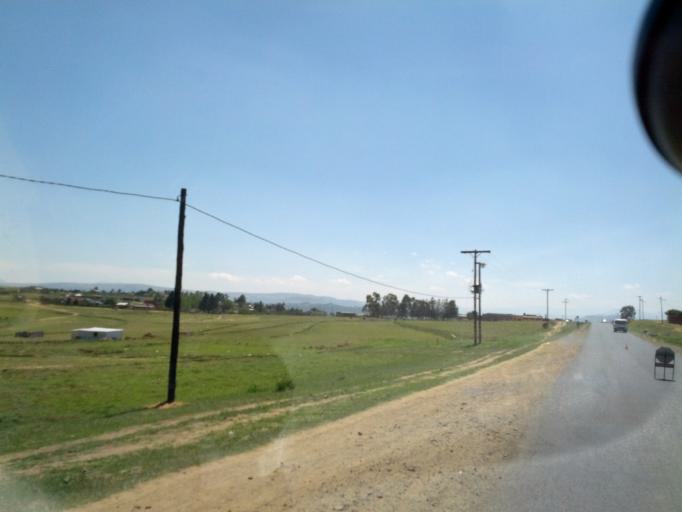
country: LS
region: Butha-Buthe
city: Butha-Buthe
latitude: -28.7802
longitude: 28.2278
